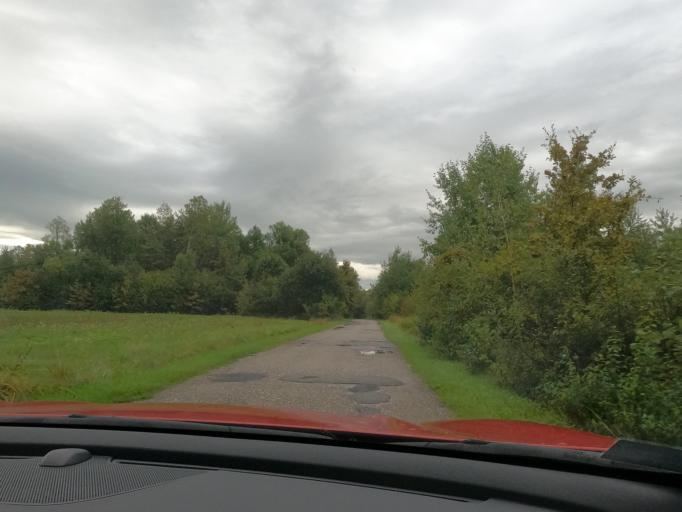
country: HR
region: Sisacko-Moslavacka
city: Petrinja
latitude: 45.3311
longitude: 16.2206
